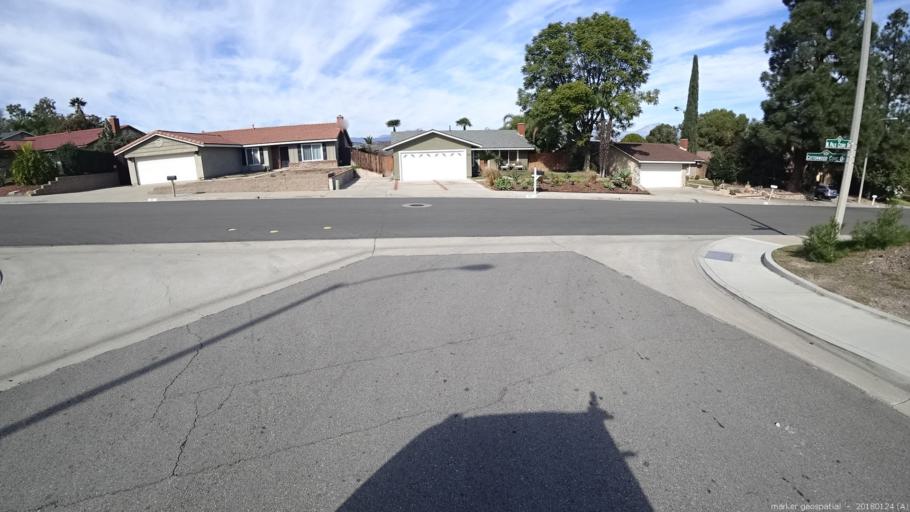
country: US
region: California
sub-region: Los Angeles County
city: Diamond Bar
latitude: 34.0255
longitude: -117.8189
